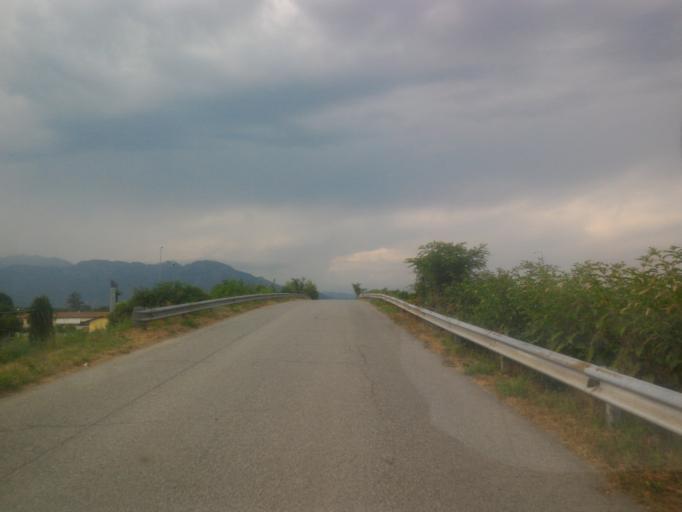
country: IT
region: Piedmont
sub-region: Provincia di Torino
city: Riva
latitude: 44.8915
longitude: 7.3956
